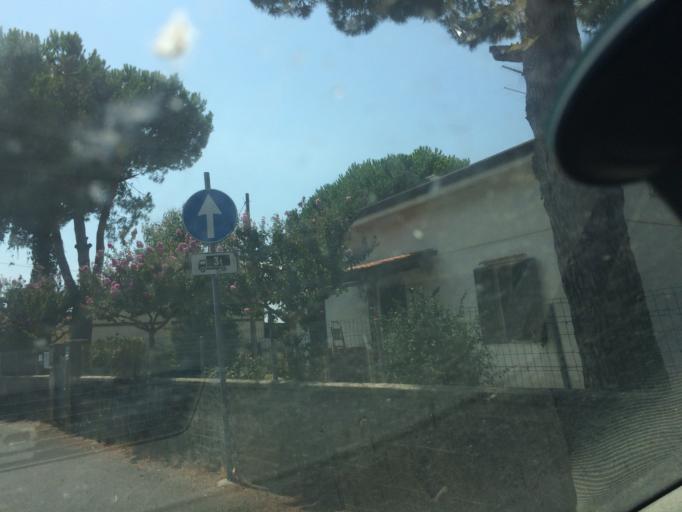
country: IT
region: Tuscany
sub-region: Provincia di Massa-Carrara
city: Massa
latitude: 44.0246
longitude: 10.0929
